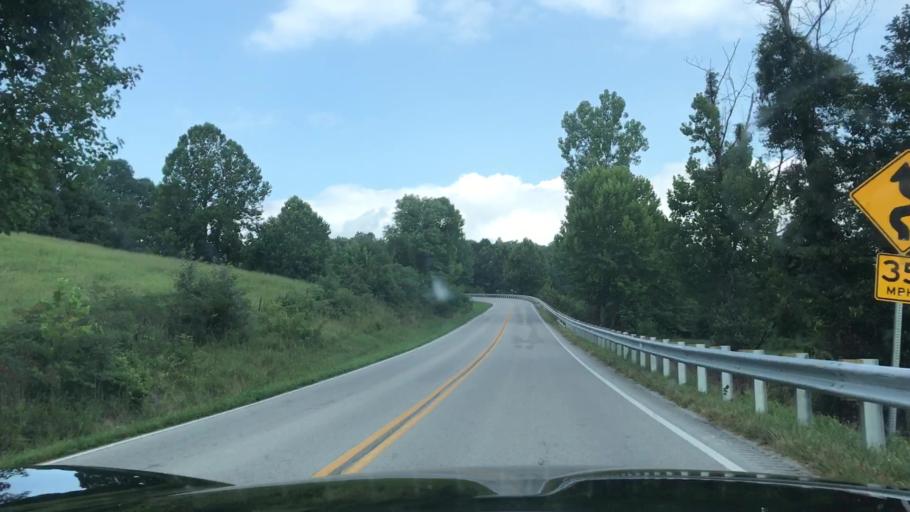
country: US
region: Kentucky
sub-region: Butler County
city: Morgantown
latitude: 37.1791
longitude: -86.8543
